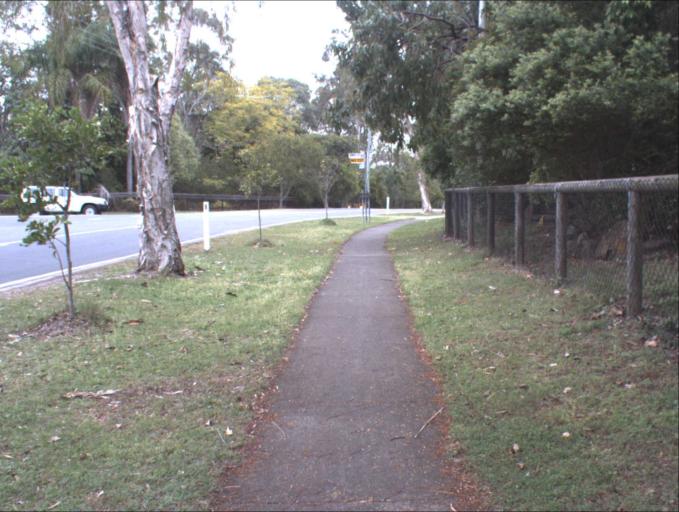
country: AU
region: Queensland
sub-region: Brisbane
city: Forest Lake
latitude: -27.6665
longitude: 153.0081
